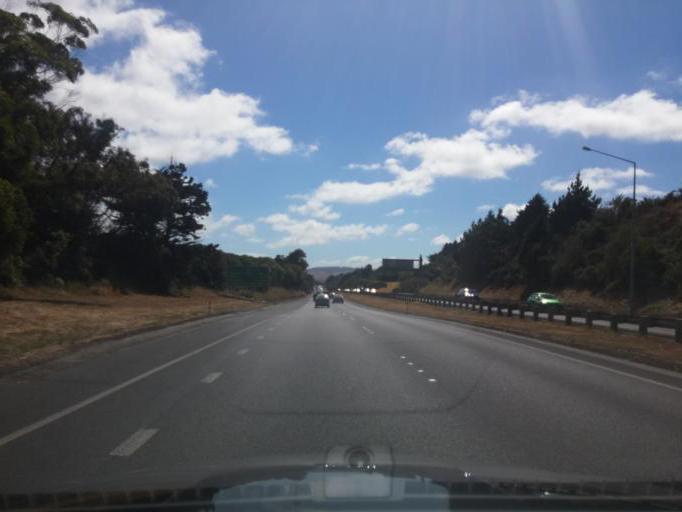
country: NZ
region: Wellington
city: Petone
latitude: -41.2184
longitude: 174.8108
